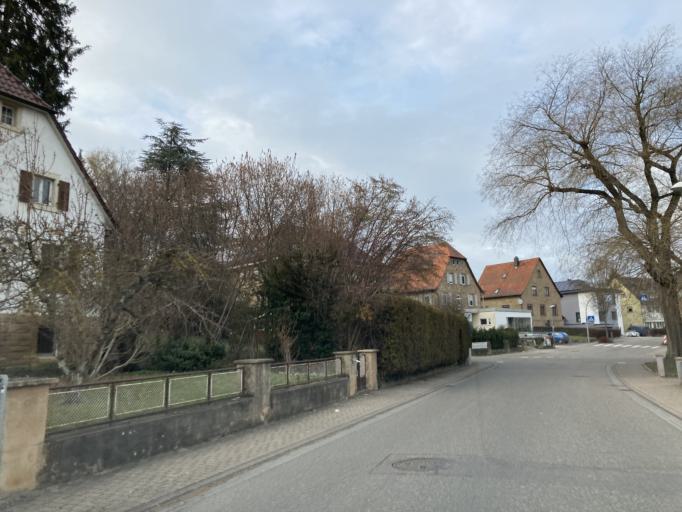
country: DE
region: Baden-Wuerttemberg
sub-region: Karlsruhe Region
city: Oberderdingen
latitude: 49.0641
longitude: 8.7972
